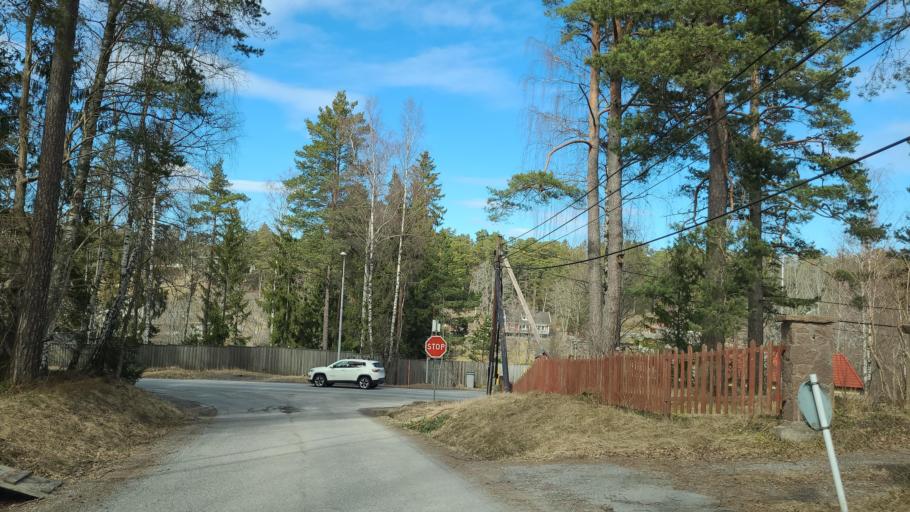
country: SE
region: Stockholm
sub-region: Varmdo Kommun
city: Hemmesta
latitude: 59.2847
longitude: 18.5516
